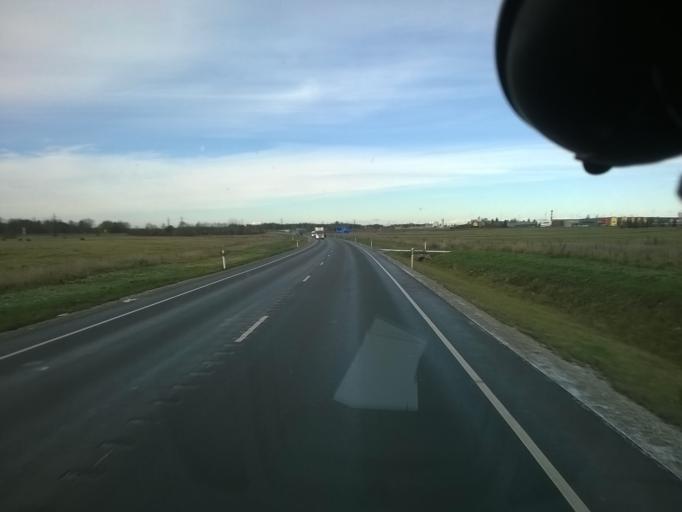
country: EE
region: Harju
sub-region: Saue vald
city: Laagri
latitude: 59.3300
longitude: 24.6302
